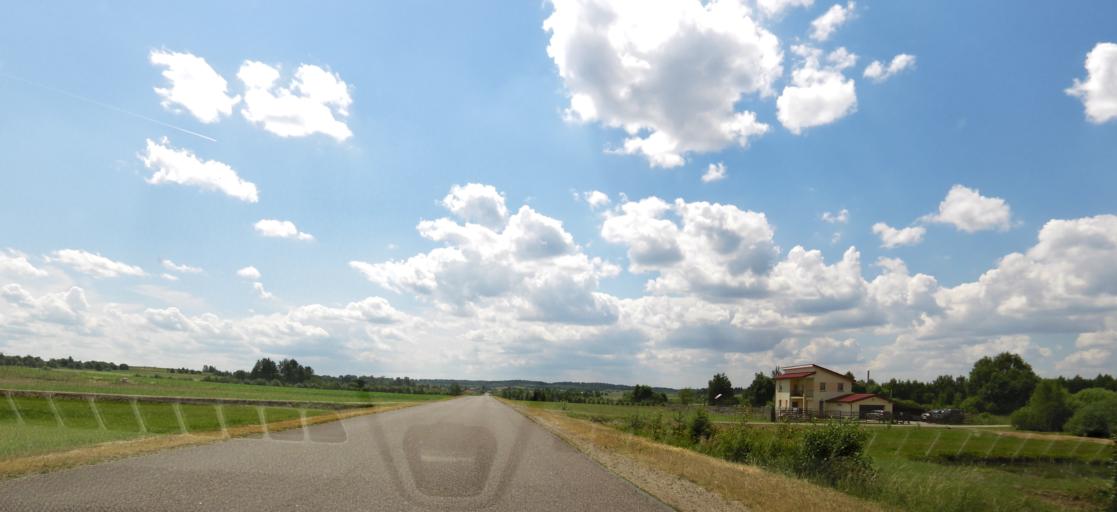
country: LT
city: Skaidiskes
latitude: 54.5536
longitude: 25.6614
